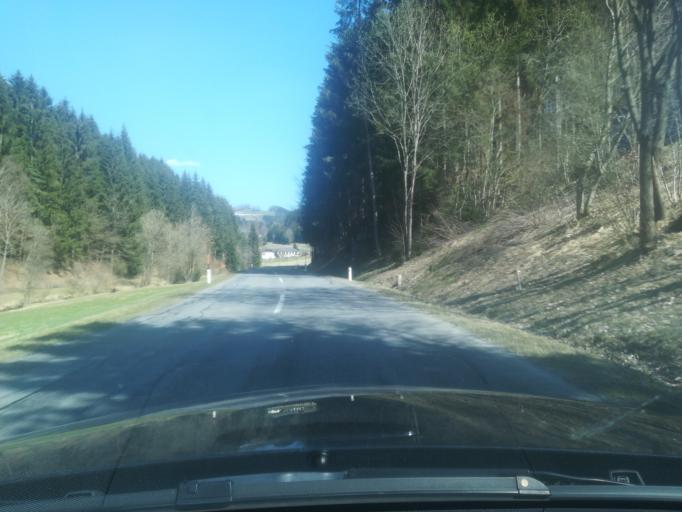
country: AT
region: Upper Austria
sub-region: Politischer Bezirk Perg
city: Sankt Georgen am Walde
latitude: 48.4529
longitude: 14.7874
